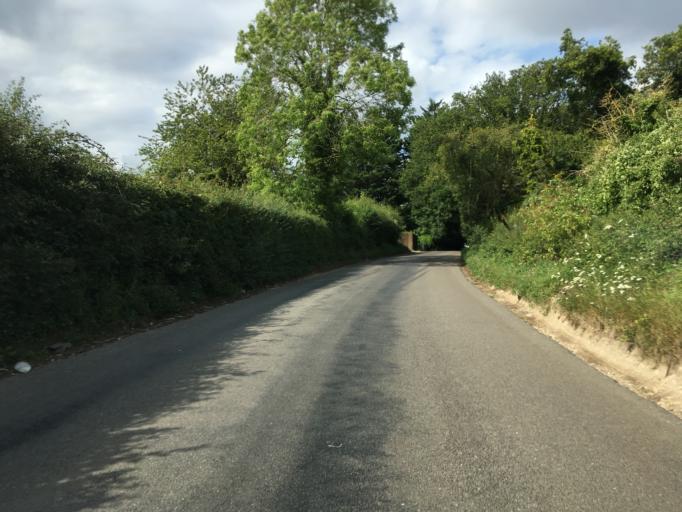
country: GB
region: England
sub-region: Hampshire
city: Overton
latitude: 51.2133
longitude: -1.2622
